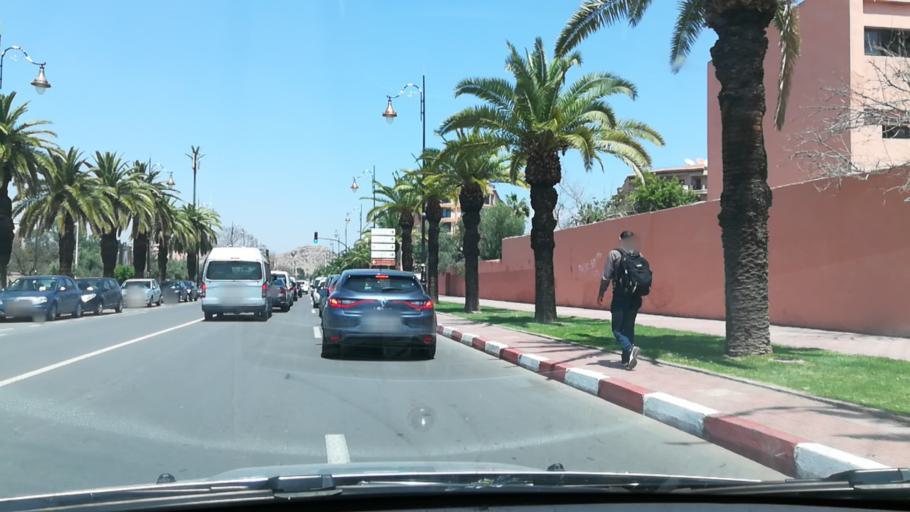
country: MA
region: Marrakech-Tensift-Al Haouz
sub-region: Marrakech
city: Marrakesh
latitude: 31.6336
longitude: -8.0183
